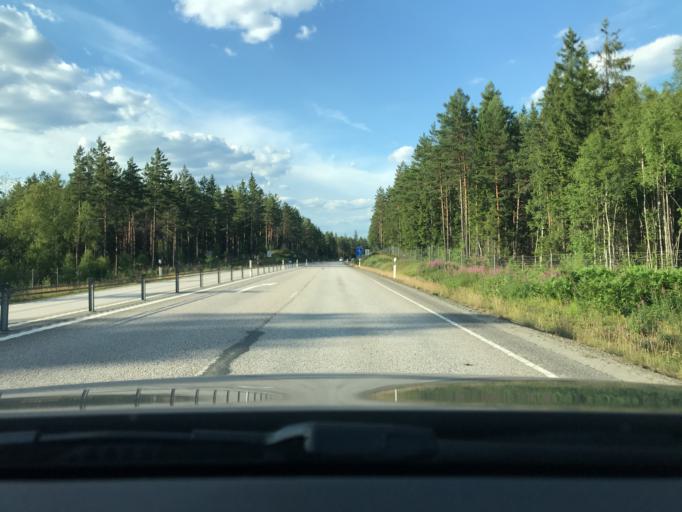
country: SE
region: Kronoberg
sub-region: Vaxjo Kommun
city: Braas
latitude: 57.0242
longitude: 15.0591
